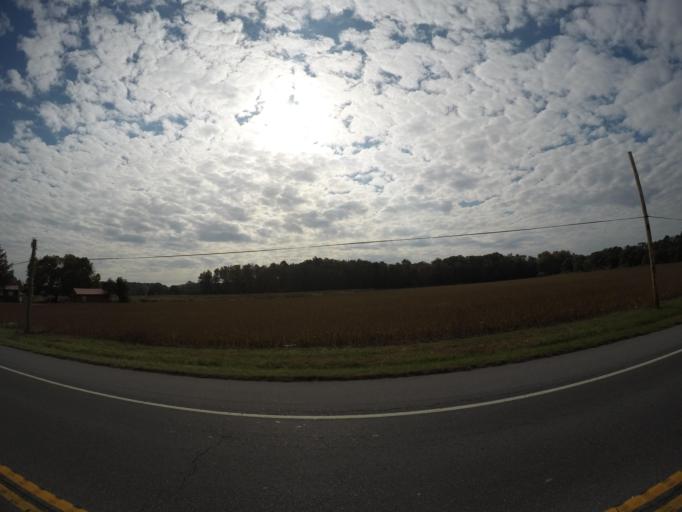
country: US
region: Delaware
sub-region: Sussex County
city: Georgetown
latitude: 38.6982
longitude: -75.4526
